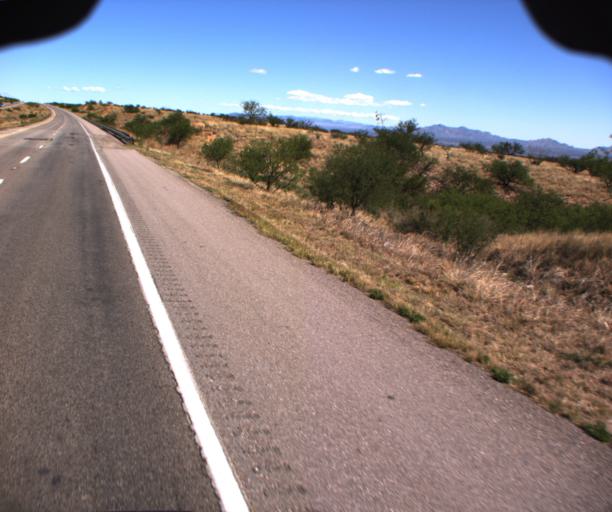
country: US
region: Arizona
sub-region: Cochise County
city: Whetstone
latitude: 31.8481
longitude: -110.3412
